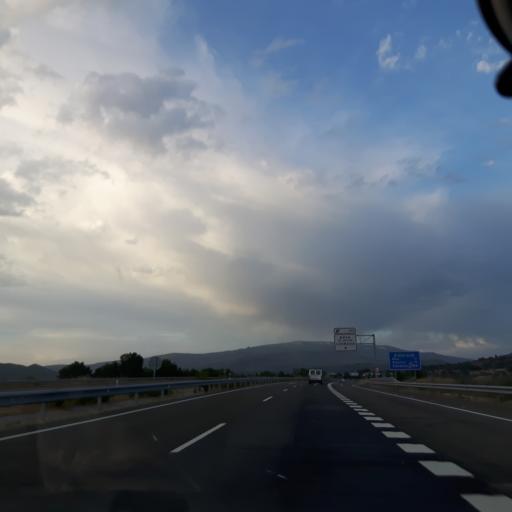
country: ES
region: Castille and Leon
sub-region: Provincia de Salamanca
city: Nava de Bejar
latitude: 40.4850
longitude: -5.6771
